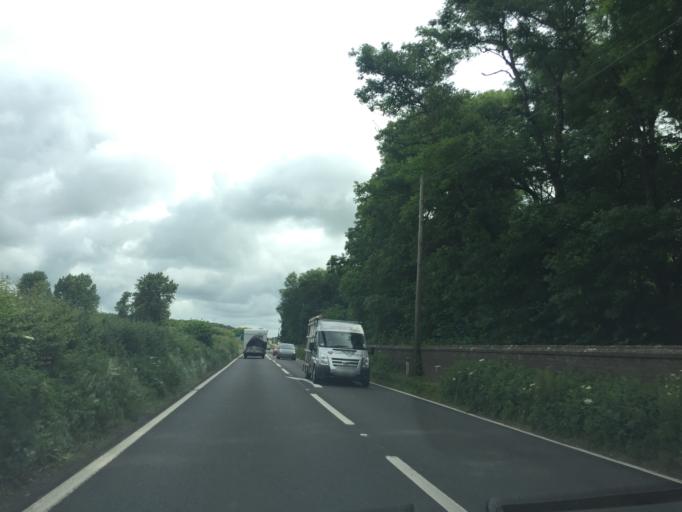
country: GB
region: England
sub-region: Dorset
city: Lytchett Matravers
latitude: 50.7915
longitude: -2.1184
